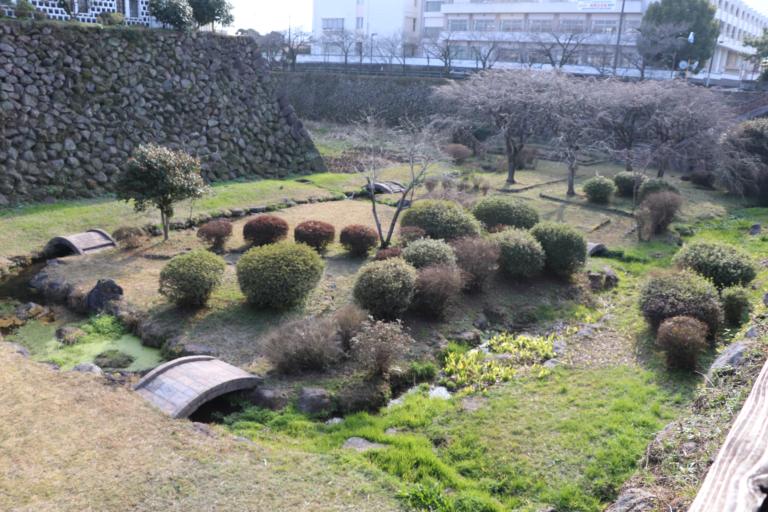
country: JP
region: Nagasaki
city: Shimabara
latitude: 32.7918
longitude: 130.3657
